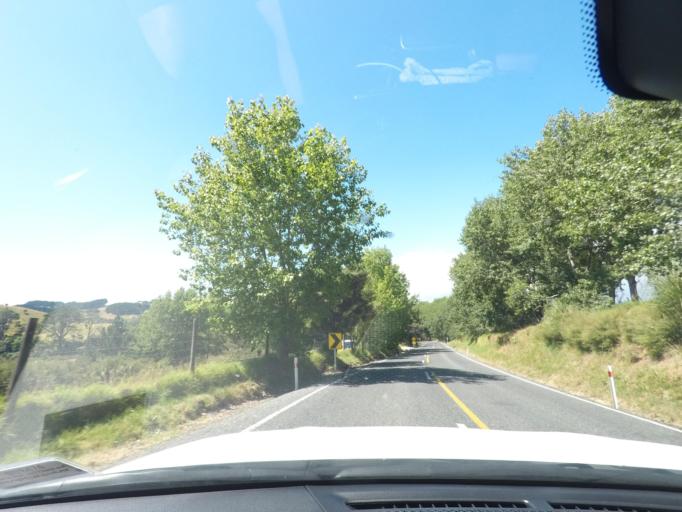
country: NZ
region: Auckland
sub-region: Auckland
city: Parakai
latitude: -36.5915
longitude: 174.3377
